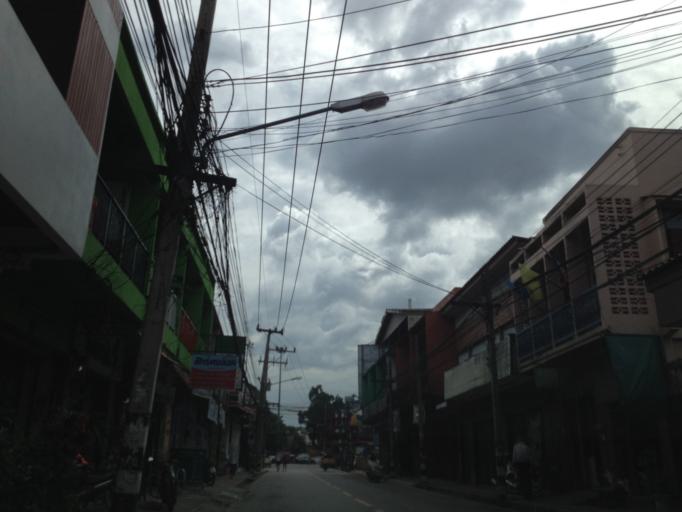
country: TH
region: Chiang Mai
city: Chiang Mai
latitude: 18.7806
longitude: 98.9872
